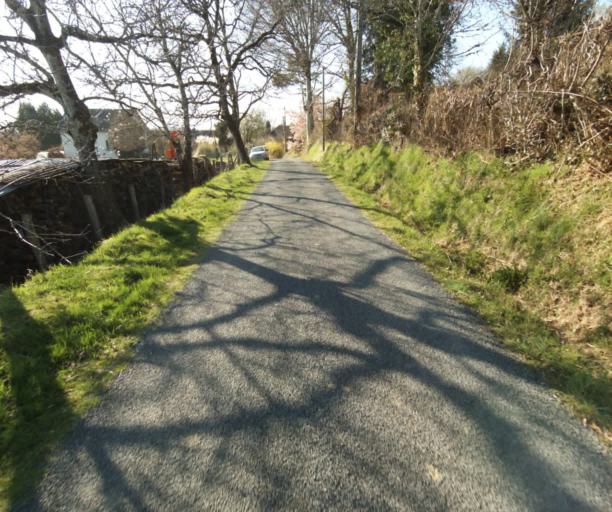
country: FR
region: Limousin
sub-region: Departement de la Correze
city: Saint-Clement
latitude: 45.3399
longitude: 1.6815
